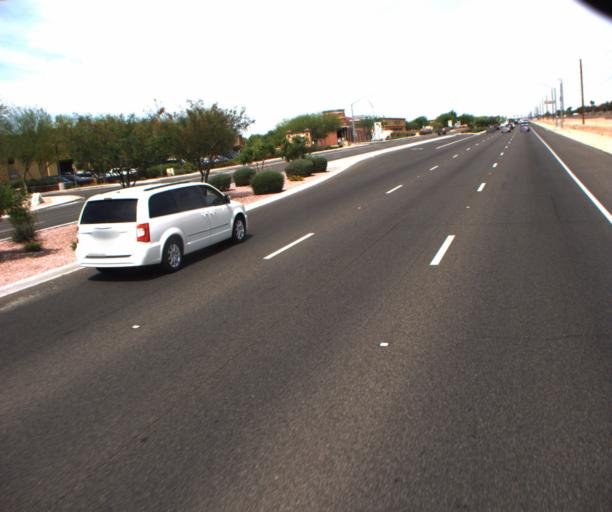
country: US
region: Arizona
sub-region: Maricopa County
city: Sun City West
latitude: 33.6503
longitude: -112.3650
